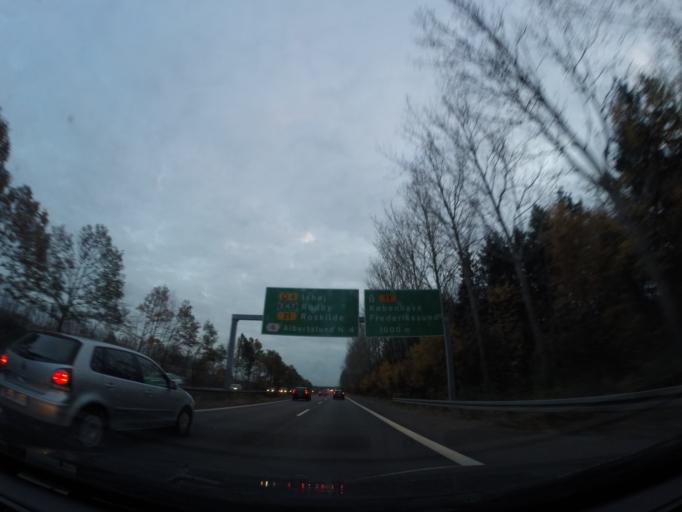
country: DK
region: Capital Region
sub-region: Ballerup Kommune
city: Ballerup
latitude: 55.7163
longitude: 12.3652
